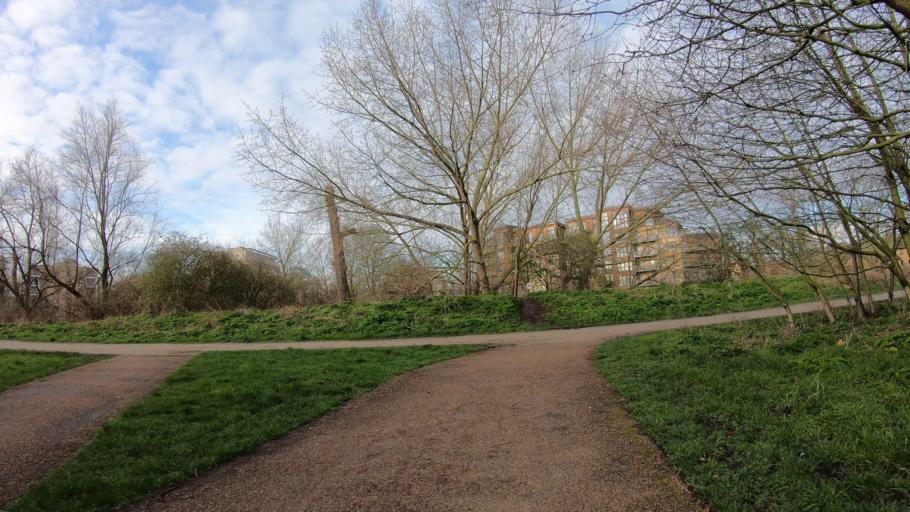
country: GB
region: England
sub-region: Greater London
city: Hackney
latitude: 51.5607
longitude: -0.0343
